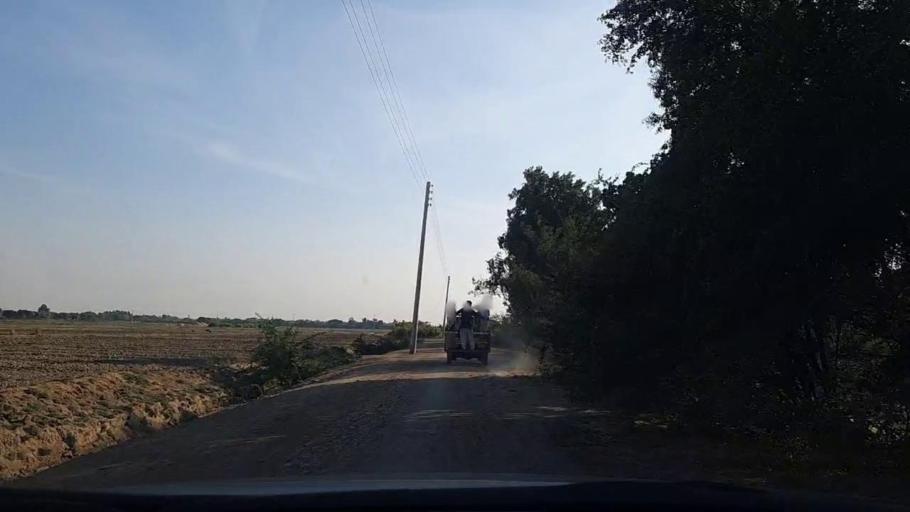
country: PK
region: Sindh
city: Mirpur Sakro
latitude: 24.5312
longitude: 67.6330
